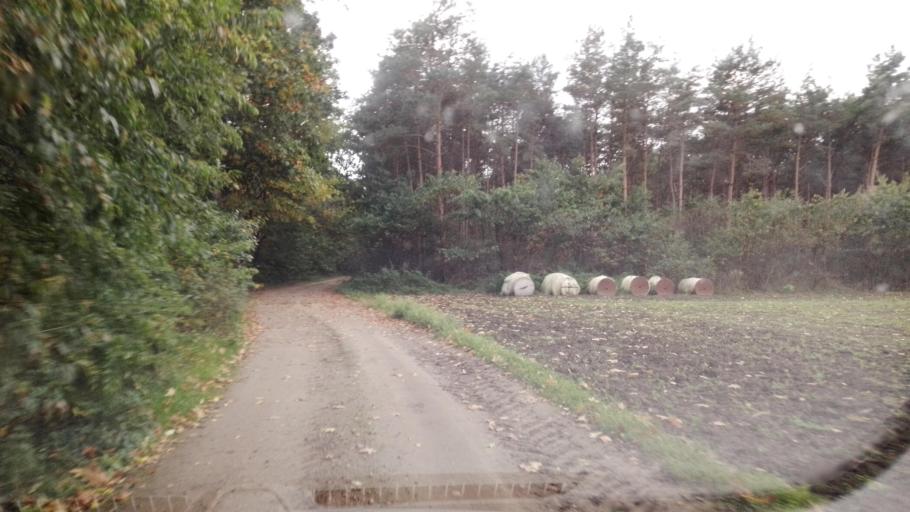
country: NL
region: Limburg
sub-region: Gemeente Venlo
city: Tegelen
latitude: 51.3973
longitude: 6.1173
